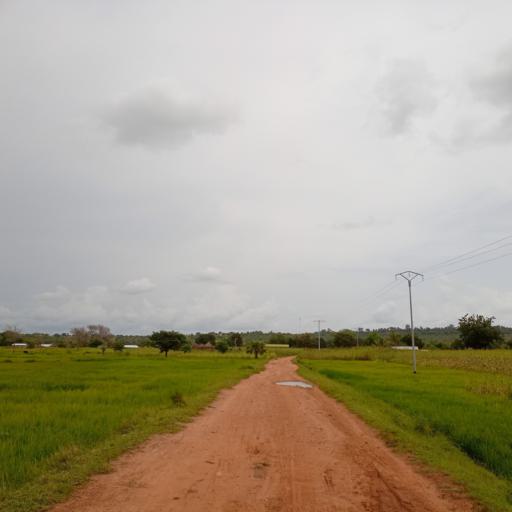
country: TG
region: Savanes
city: Dapaong
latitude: 10.8054
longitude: 0.0286
